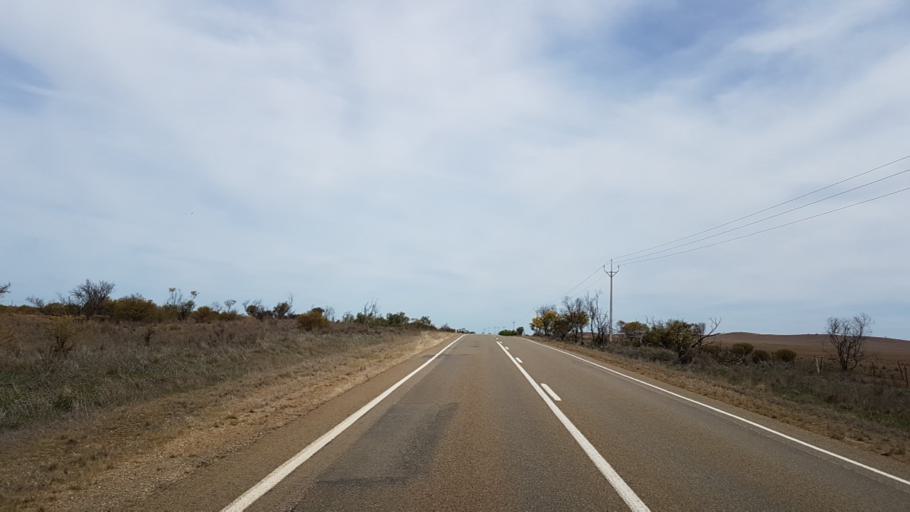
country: AU
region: South Australia
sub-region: Peterborough
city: Peterborough
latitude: -33.0094
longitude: 138.7666
